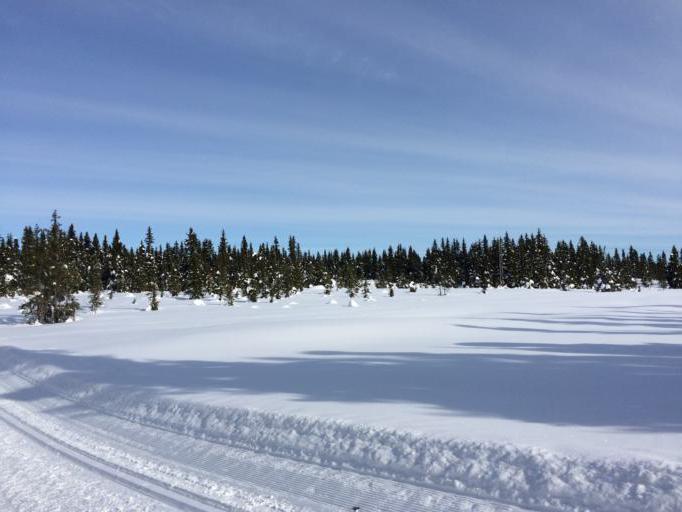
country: NO
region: Oppland
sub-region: Gausdal
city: Segalstad bru
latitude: 61.3307
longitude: 10.0832
